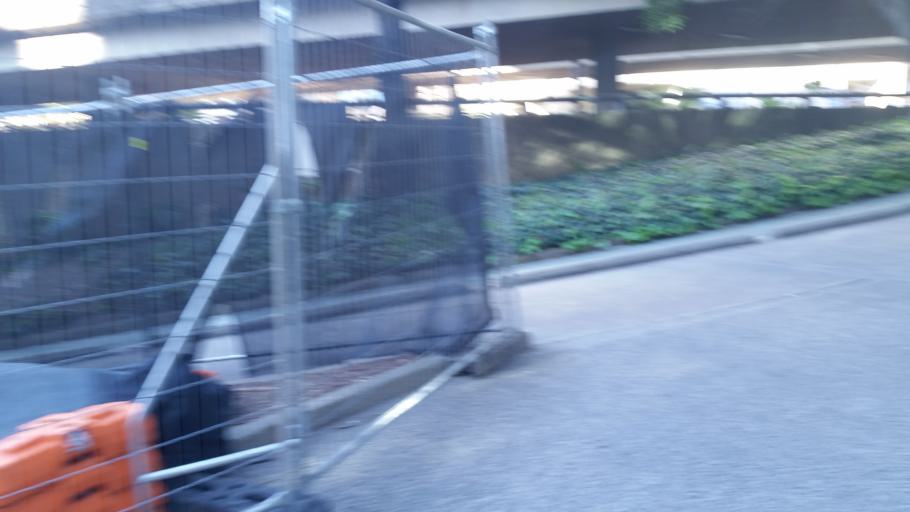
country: AU
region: New South Wales
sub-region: City of Sydney
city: Sydney
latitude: -33.8634
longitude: 151.2041
